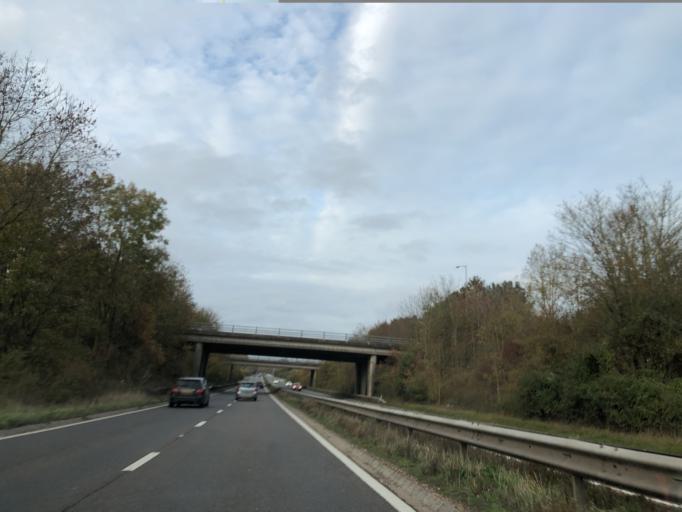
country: GB
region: England
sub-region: Buckinghamshire
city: Marlow
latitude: 51.5797
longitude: -0.7565
